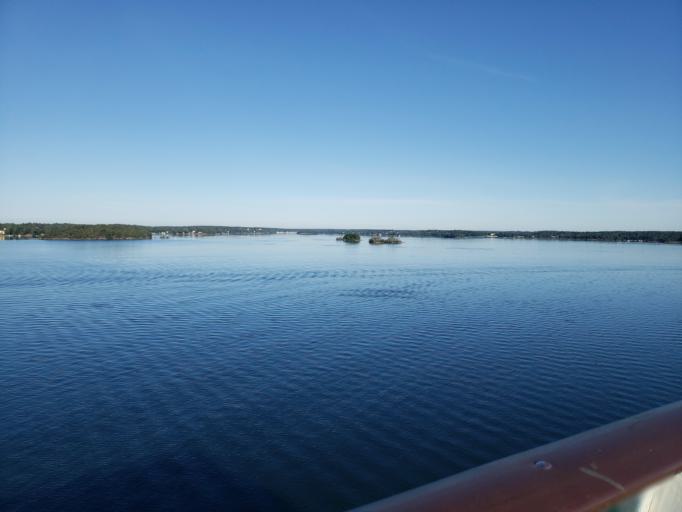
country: SE
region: Stockholm
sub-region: Vaxholms Kommun
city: Vaxholm
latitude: 59.4346
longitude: 18.3829
